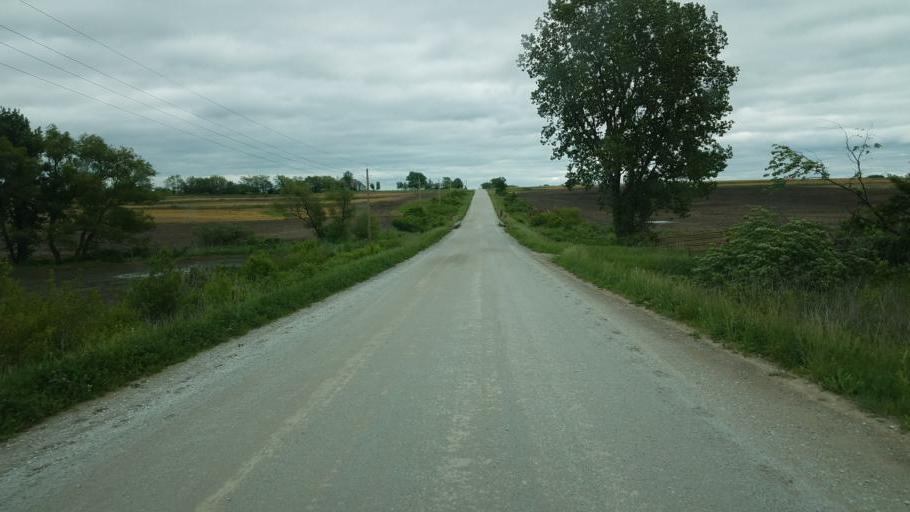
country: US
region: Iowa
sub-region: Decatur County
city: Lamoni
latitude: 40.6382
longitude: -93.9155
